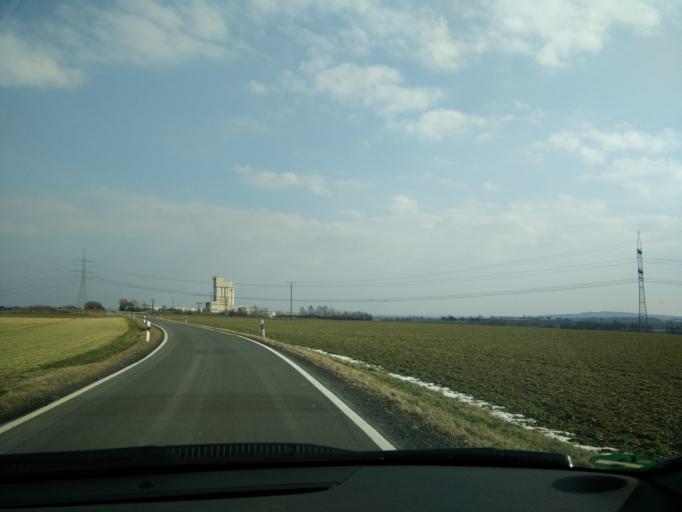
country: DE
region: Saxony
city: Konigsfeld
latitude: 51.1025
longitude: 12.7394
